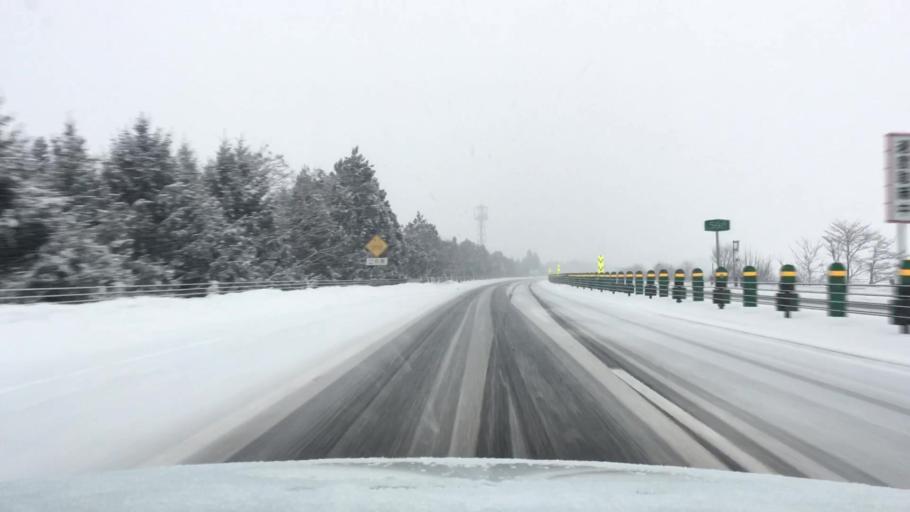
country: JP
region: Akita
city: Hanawa
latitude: 40.2196
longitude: 140.7926
